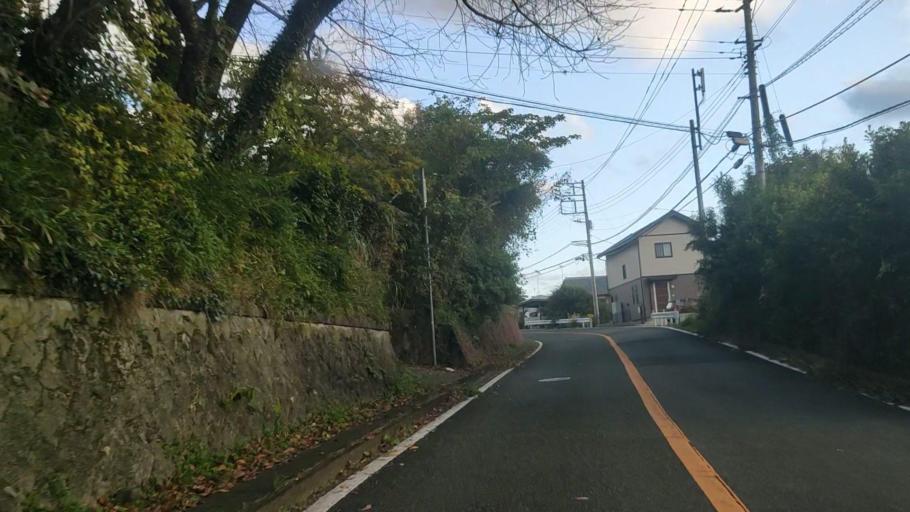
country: JP
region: Shizuoka
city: Ito
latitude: 34.9568
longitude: 139.0808
